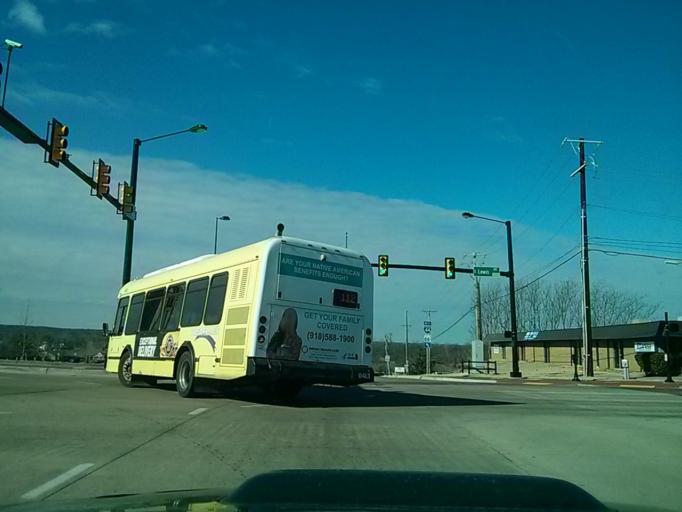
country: US
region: Oklahoma
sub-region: Tulsa County
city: Jenks
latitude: 36.0911
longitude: -95.9578
